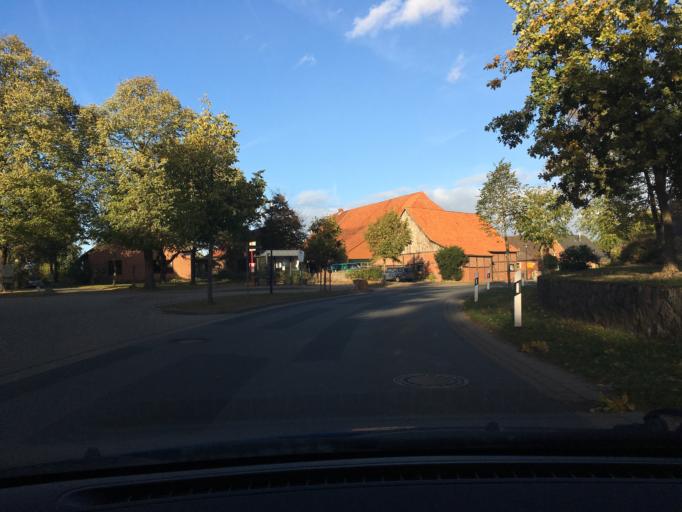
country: DE
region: Lower Saxony
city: Hittbergen
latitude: 53.3443
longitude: 10.5886
